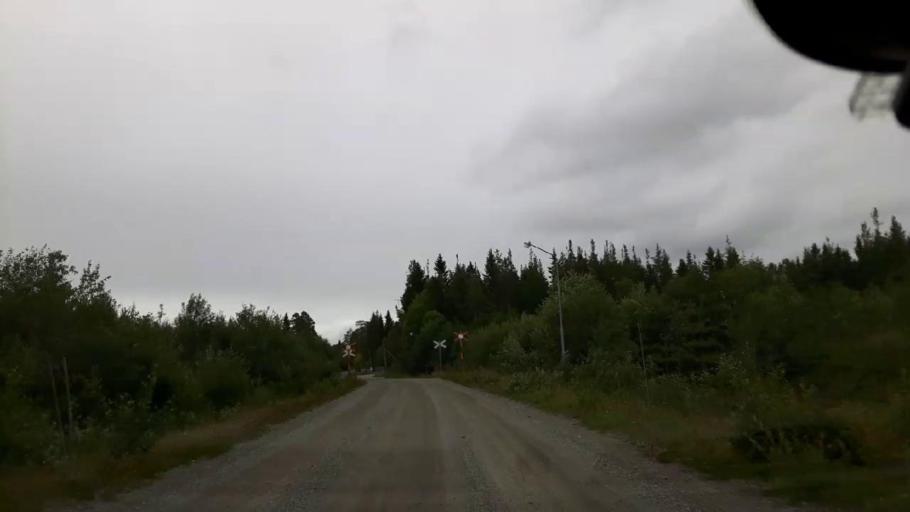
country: SE
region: Jaemtland
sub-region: Bergs Kommun
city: Hoverberg
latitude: 62.7951
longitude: 14.4786
